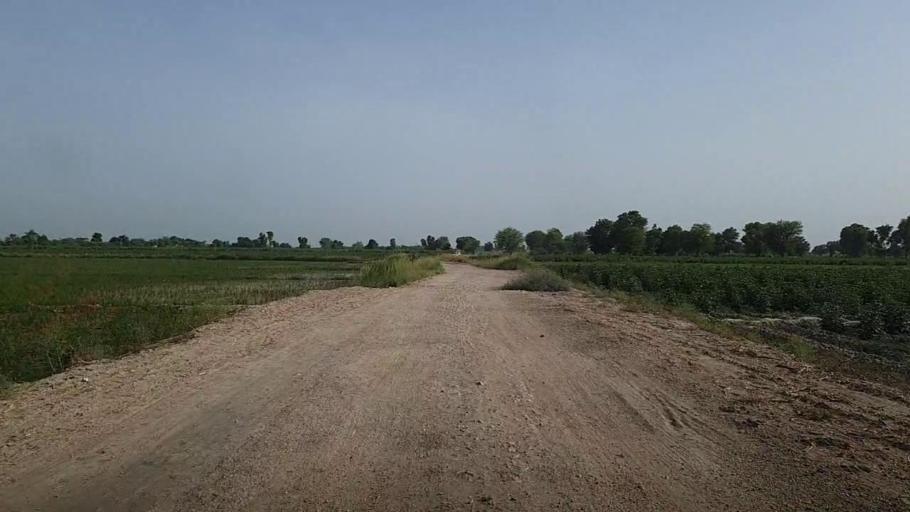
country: PK
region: Sindh
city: Pad Idan
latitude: 26.7575
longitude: 68.2572
